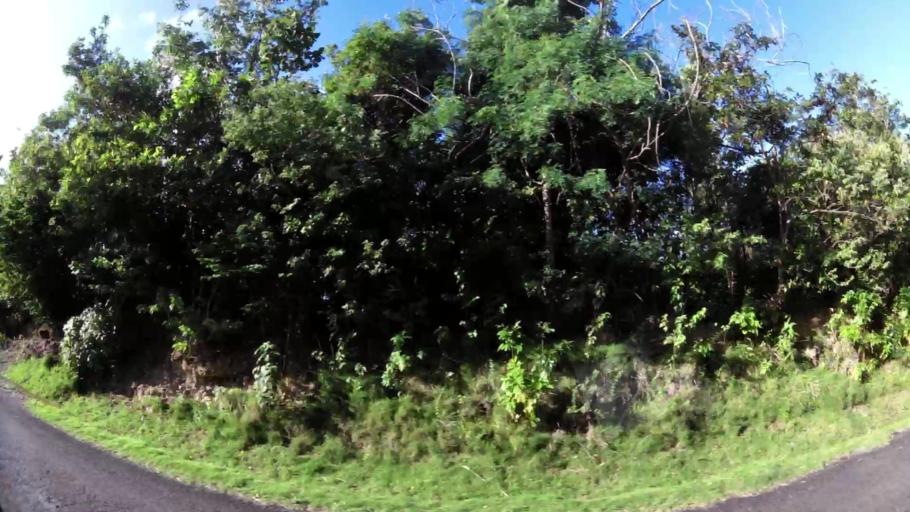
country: LC
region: Anse-la-Raye
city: Anse La Raye
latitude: 13.9224
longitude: -61.0424
